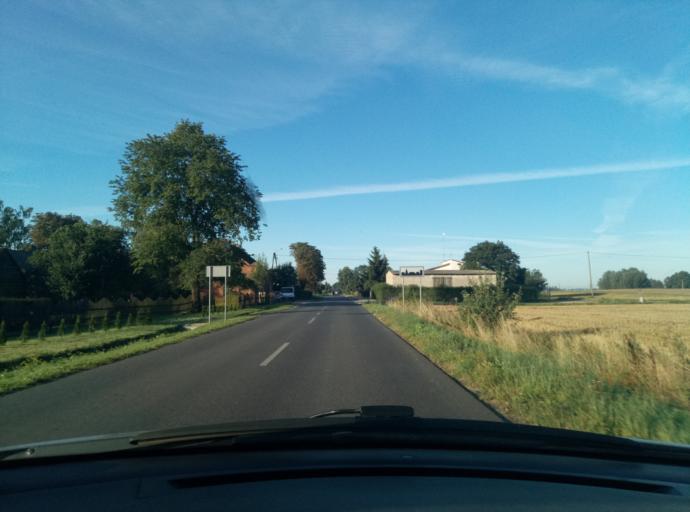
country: PL
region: Kujawsko-Pomorskie
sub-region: Powiat golubsko-dobrzynski
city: Kowalewo Pomorskie
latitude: 53.2047
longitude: 18.9191
